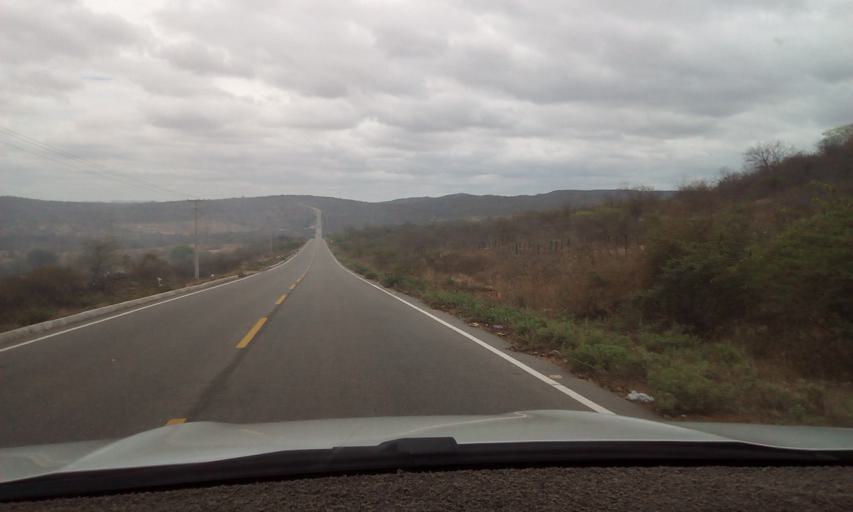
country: BR
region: Paraiba
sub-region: Picui
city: Picui
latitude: -6.5428
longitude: -36.3008
